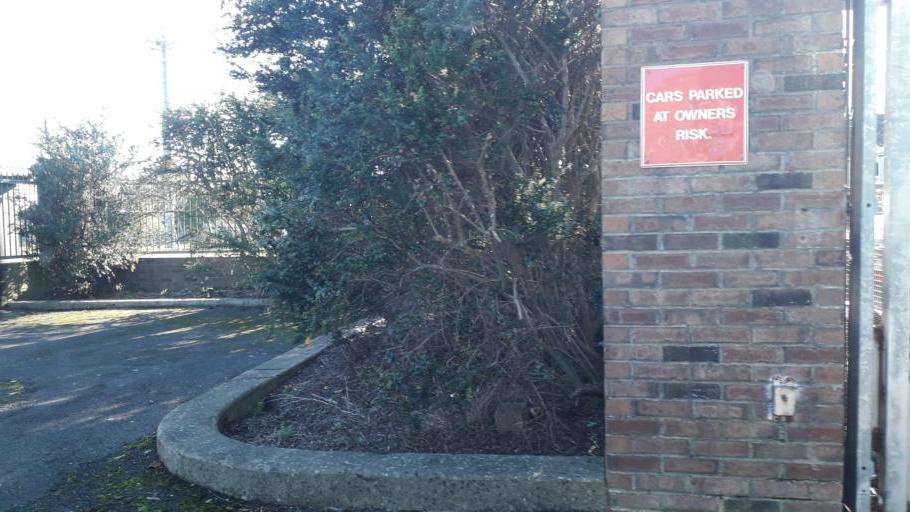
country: IE
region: Leinster
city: Raheny
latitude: 53.3887
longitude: -6.1791
